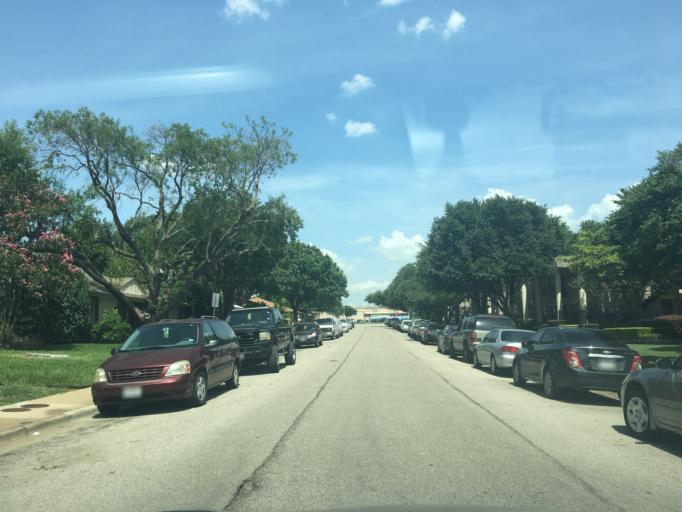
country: US
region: Texas
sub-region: Dallas County
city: Farmers Branch
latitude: 32.9119
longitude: -96.8534
